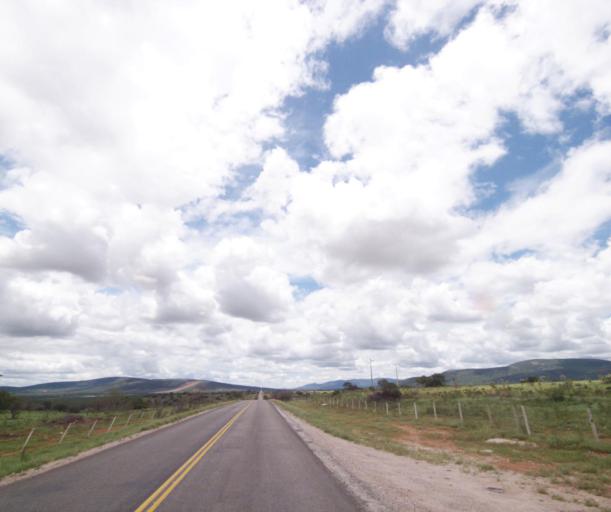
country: BR
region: Bahia
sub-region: Brumado
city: Brumado
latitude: -14.1545
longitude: -41.5155
